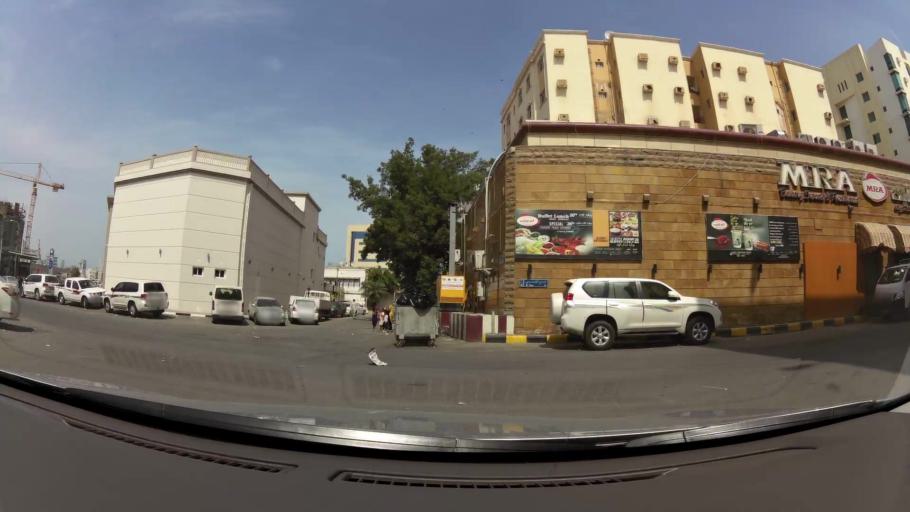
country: QA
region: Baladiyat ad Dawhah
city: Doha
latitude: 25.2804
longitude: 51.5368
